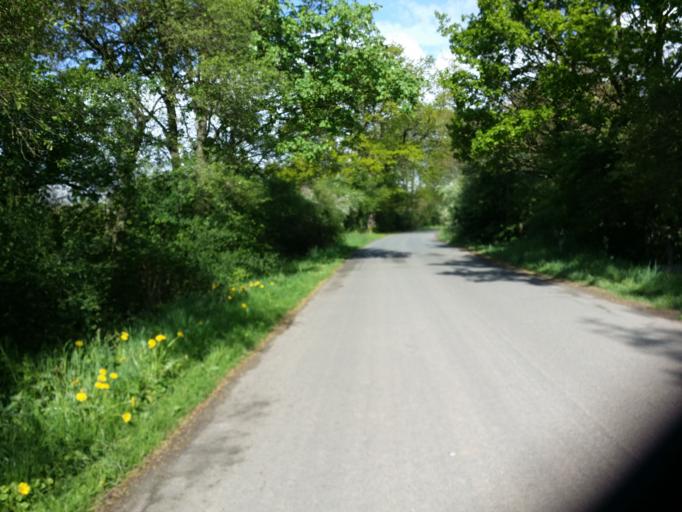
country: DE
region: Lower Saxony
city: Ahsen-Oetzen
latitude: 52.9788
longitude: 9.1139
